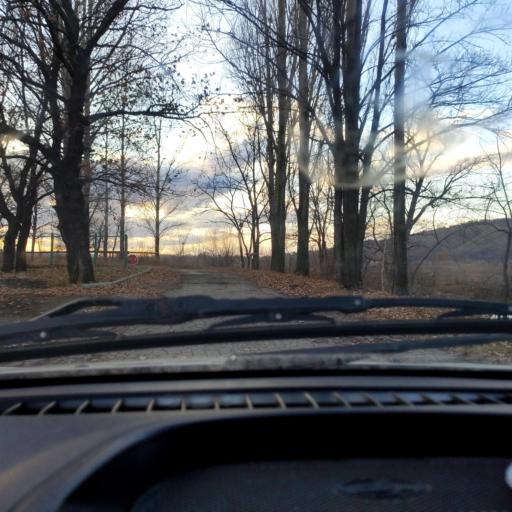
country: RU
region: Samara
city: Povolzhskiy
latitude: 53.4678
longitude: 49.6875
